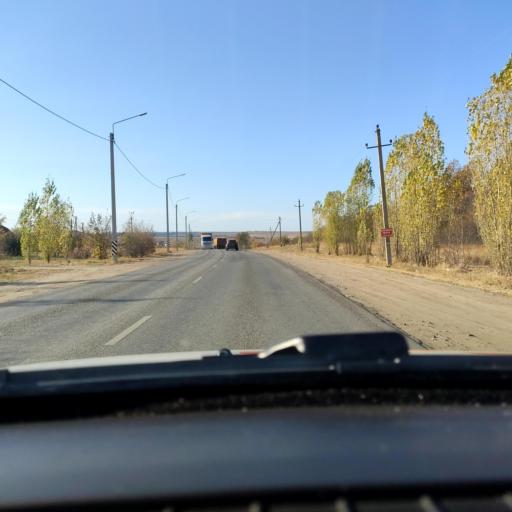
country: RU
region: Voronezj
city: Semiluki
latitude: 51.7268
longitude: 39.0315
